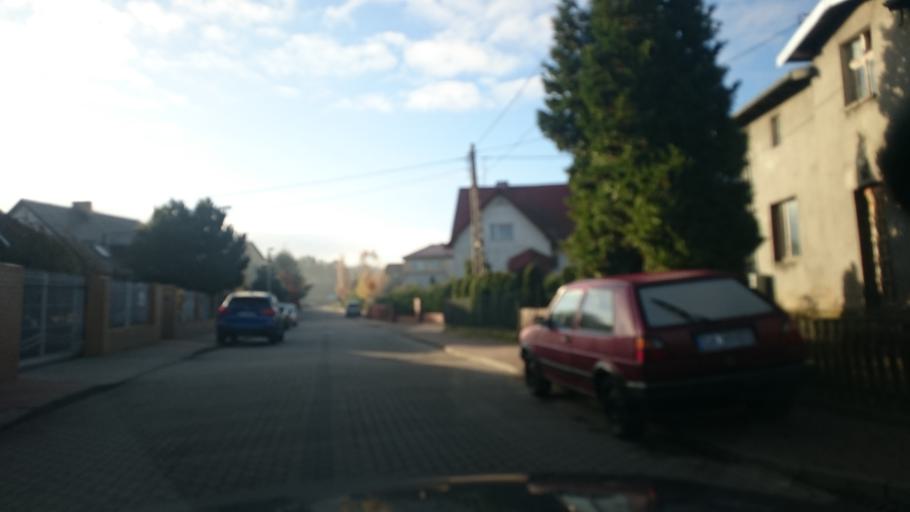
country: PL
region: Pomeranian Voivodeship
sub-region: Gdynia
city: Wielki Kack
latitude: 54.4630
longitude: 18.4934
